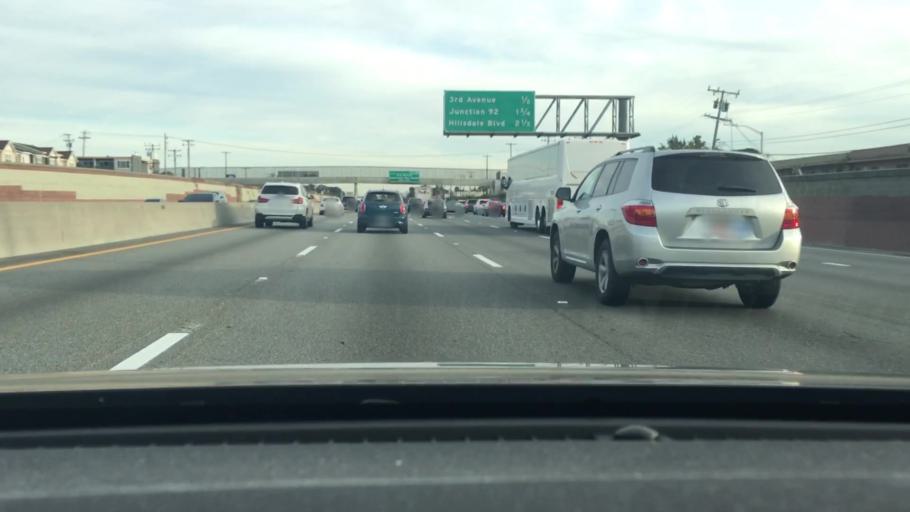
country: US
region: California
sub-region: San Mateo County
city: San Mateo
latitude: 37.5786
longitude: -122.3214
